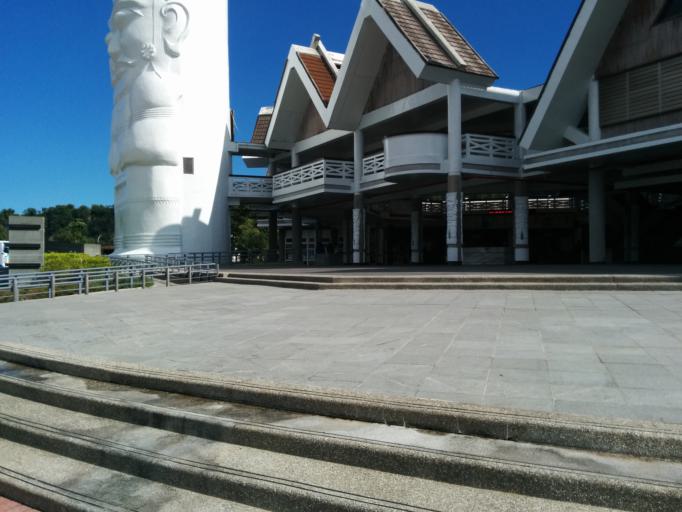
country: TW
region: Taiwan
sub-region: Hualien
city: Hualian
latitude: 23.4881
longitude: 121.4008
